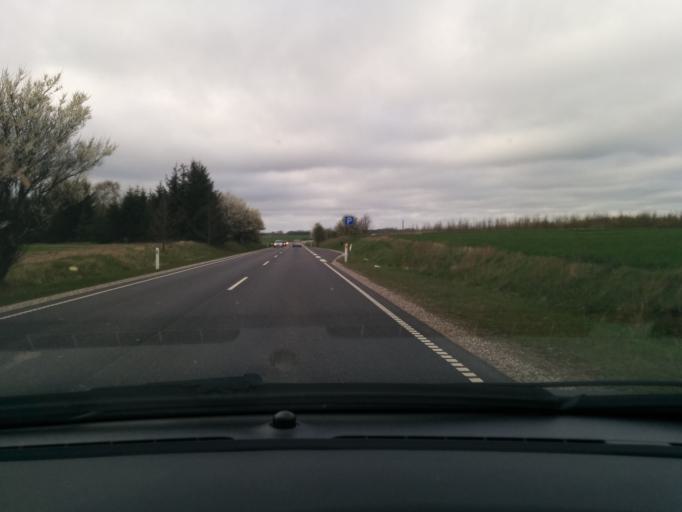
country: DK
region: Central Jutland
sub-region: Favrskov Kommune
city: Hammel
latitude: 56.2190
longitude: 9.8503
